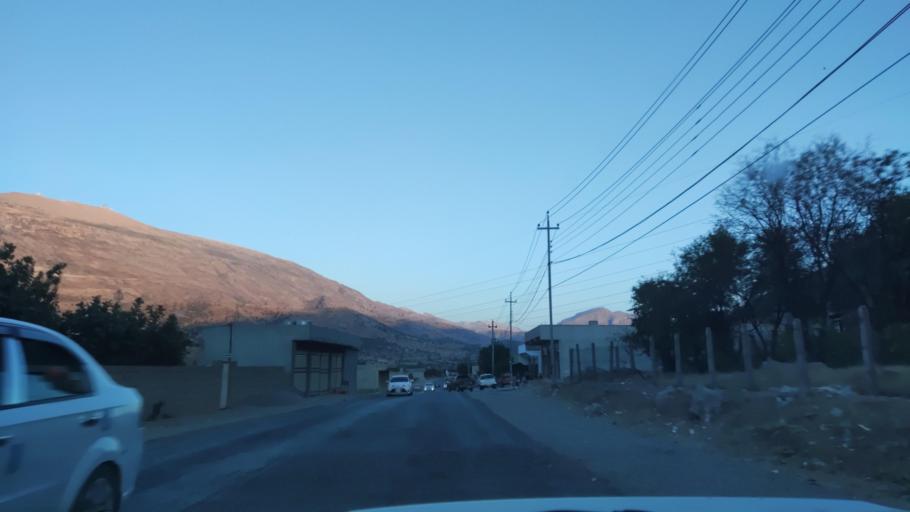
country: IQ
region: Arbil
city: Ruwandiz
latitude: 36.5897
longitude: 44.3906
